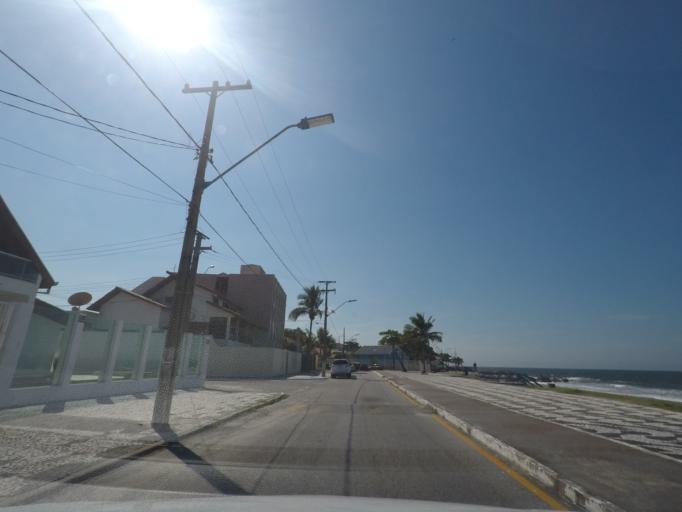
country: BR
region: Parana
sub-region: Guaratuba
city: Guaratuba
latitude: -25.8201
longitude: -48.5310
